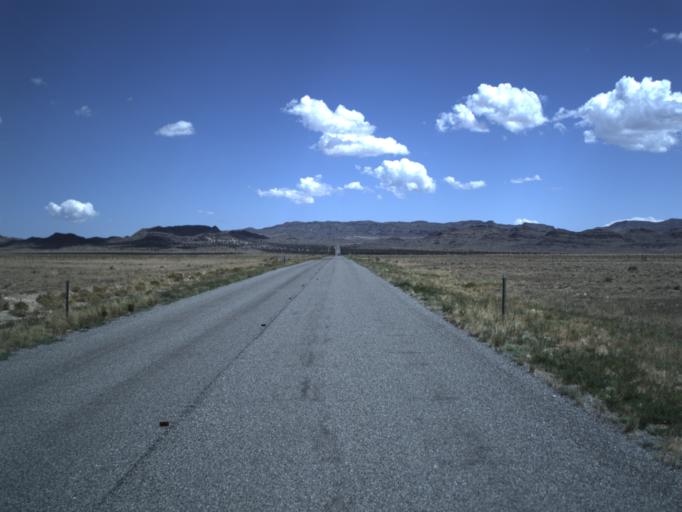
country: US
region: Utah
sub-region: Beaver County
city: Milford
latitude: 39.0544
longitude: -113.7731
